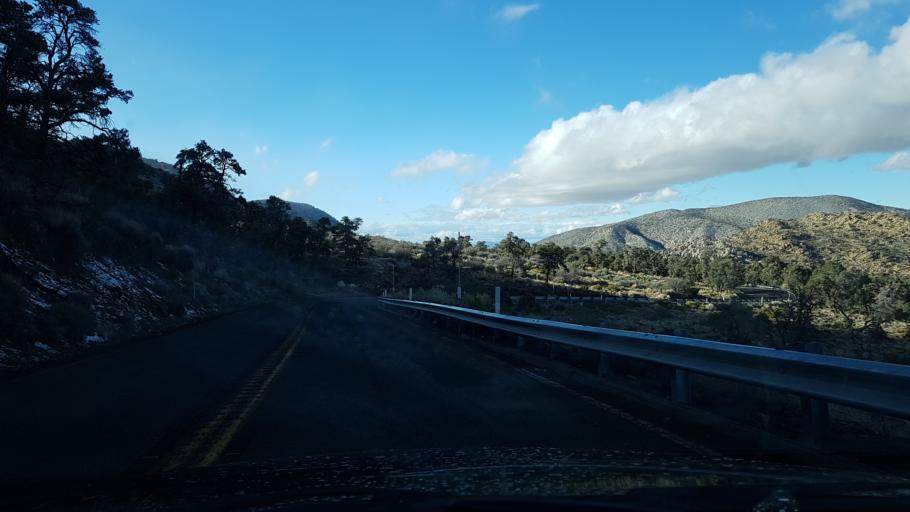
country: US
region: California
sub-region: San Bernardino County
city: Big Bear City
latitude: 34.3038
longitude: -116.8038
